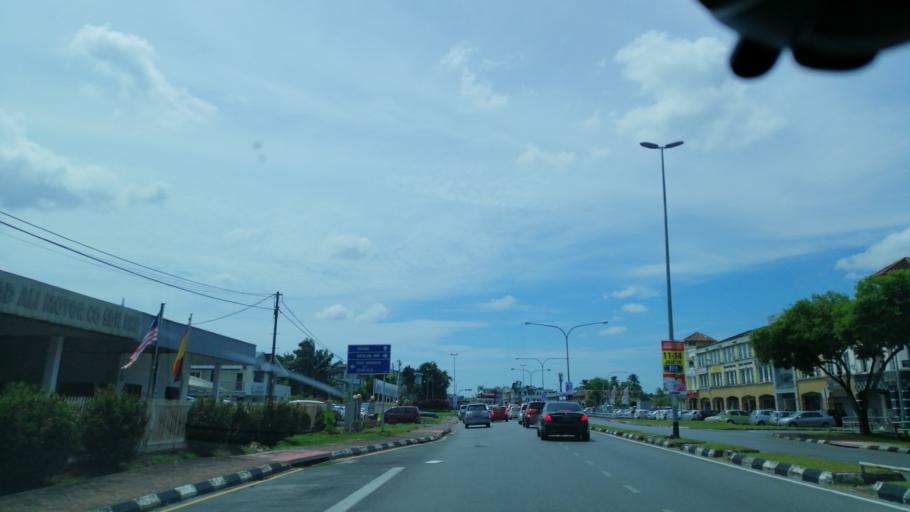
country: MY
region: Sarawak
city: Kuching
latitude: 1.5445
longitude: 110.3602
